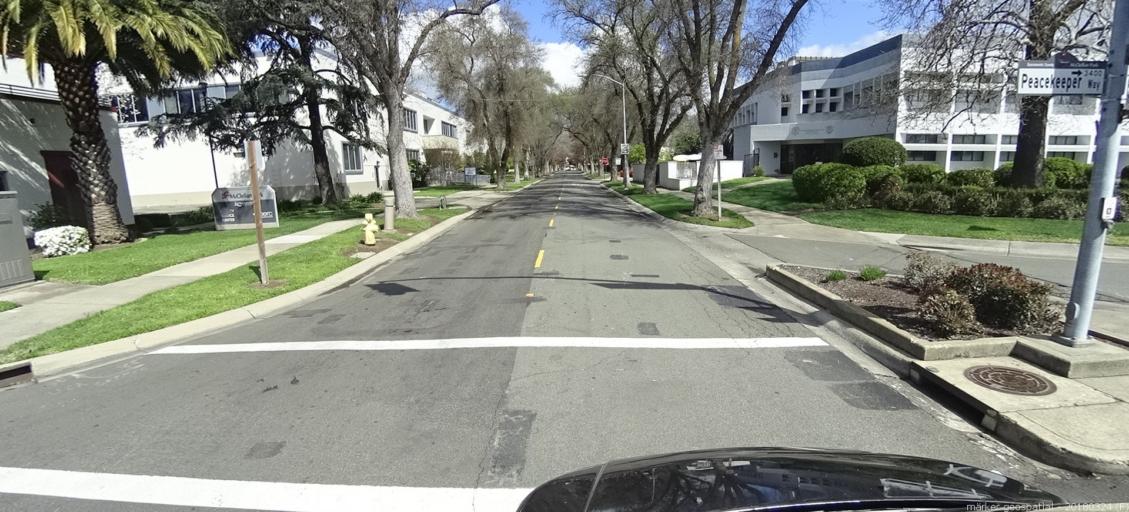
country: US
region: California
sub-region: Sacramento County
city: North Highlands
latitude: 38.6608
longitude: -121.3852
